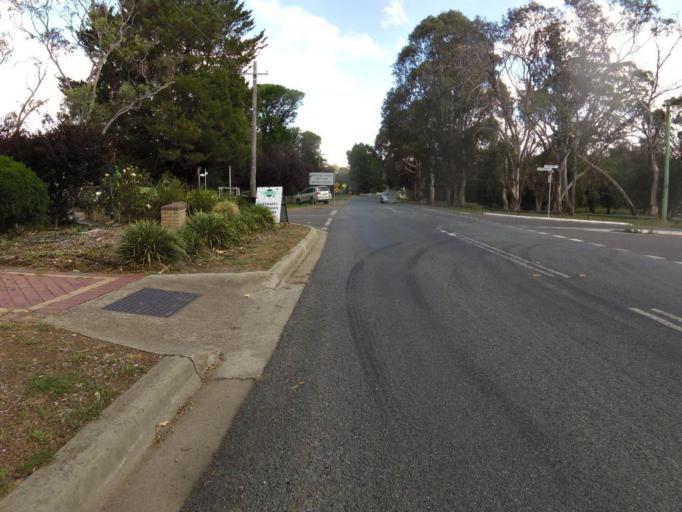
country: AU
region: Australian Capital Territory
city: Belconnen
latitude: -35.1709
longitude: 149.0704
